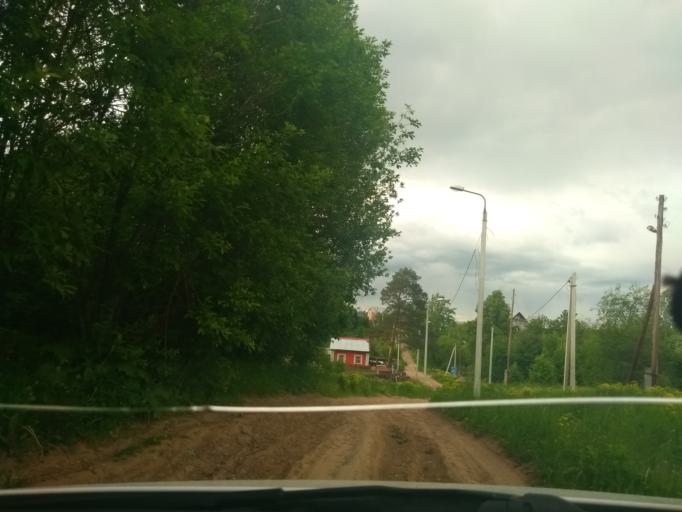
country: RU
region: Perm
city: Perm
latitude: 57.9888
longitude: 56.3366
